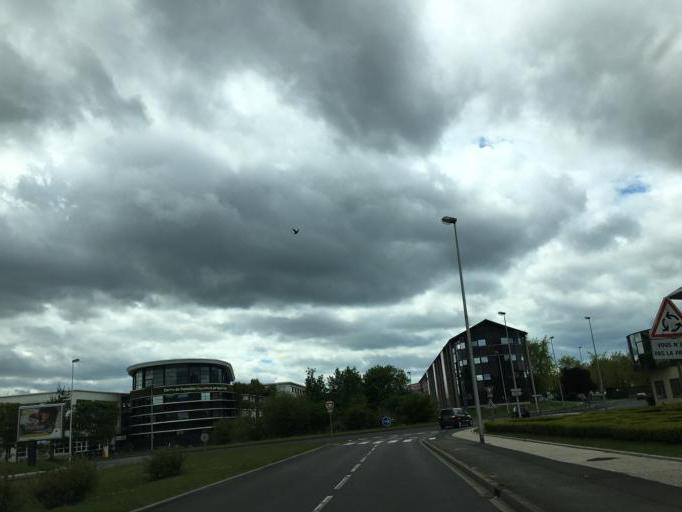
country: FR
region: Centre
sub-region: Departement du Loiret
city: Fleury-les-Aubrais
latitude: 47.9194
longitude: 1.9247
